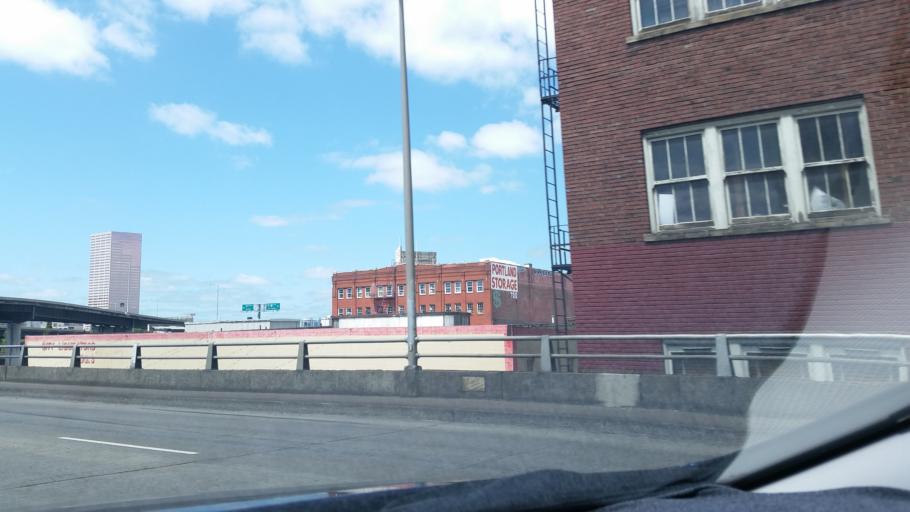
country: US
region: Oregon
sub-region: Multnomah County
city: Portland
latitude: 45.5172
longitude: -122.6635
